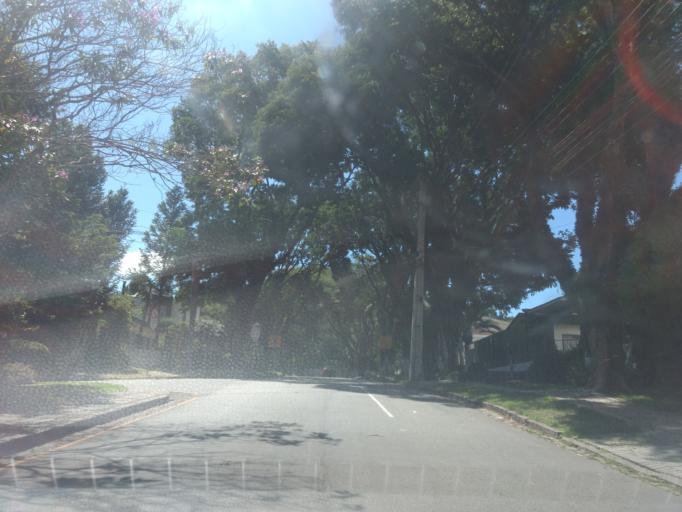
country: BR
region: Parana
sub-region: Curitiba
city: Curitiba
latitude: -25.4106
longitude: -49.2341
